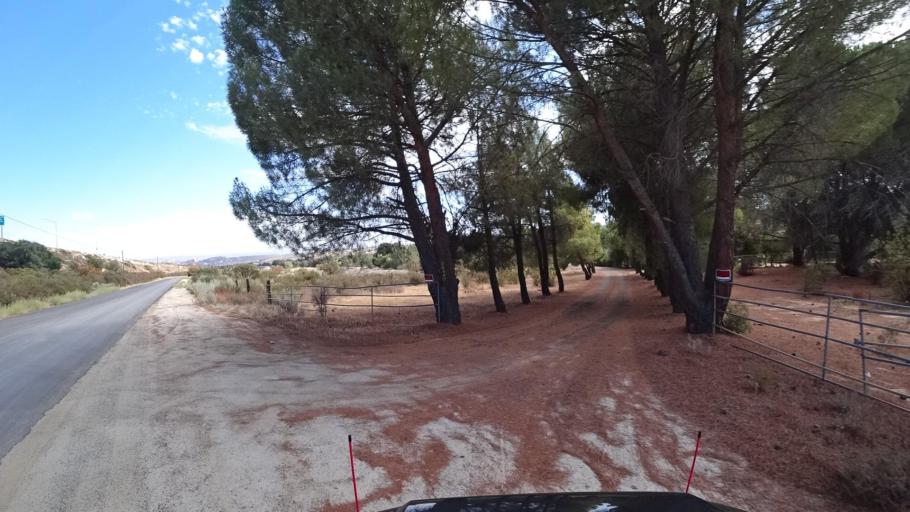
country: US
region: California
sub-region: San Diego County
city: Campo
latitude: 32.6803
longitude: -116.2972
